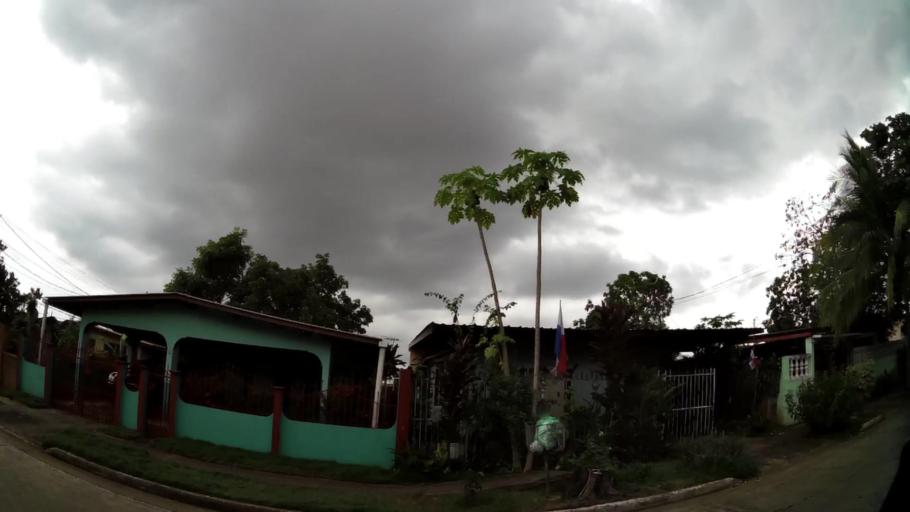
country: PA
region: Panama
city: Tocumen
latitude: 9.0510
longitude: -79.4126
